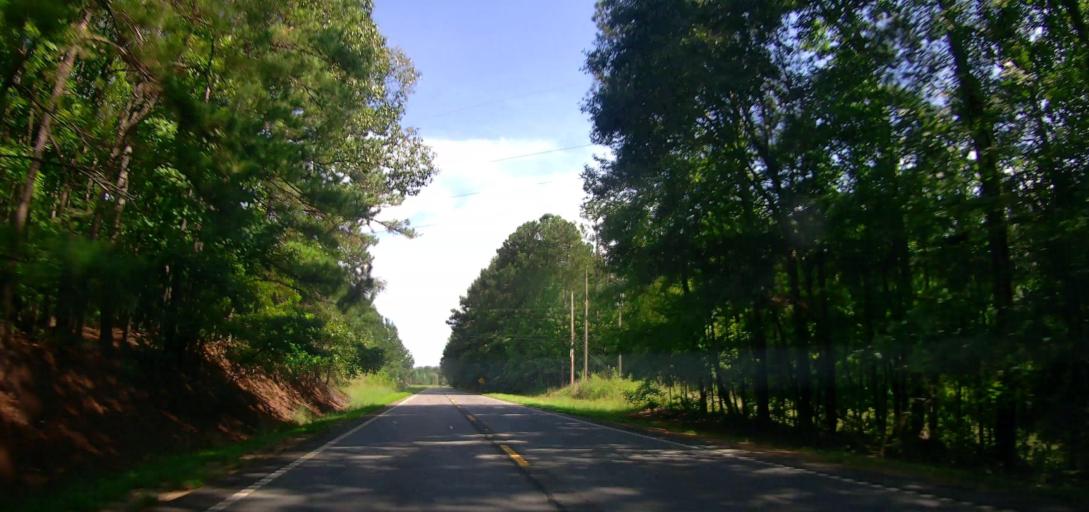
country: US
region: Georgia
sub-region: Talbot County
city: Sardis
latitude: 32.8192
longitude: -84.6071
